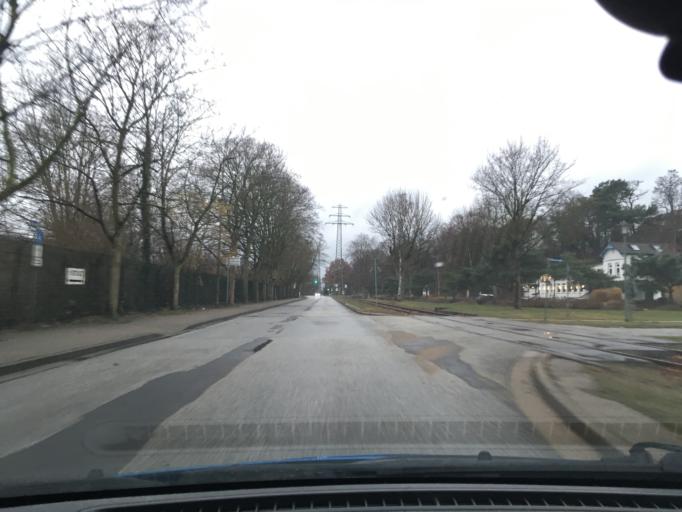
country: DE
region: Schleswig-Holstein
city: Geesthacht
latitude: 53.4269
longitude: 10.3767
